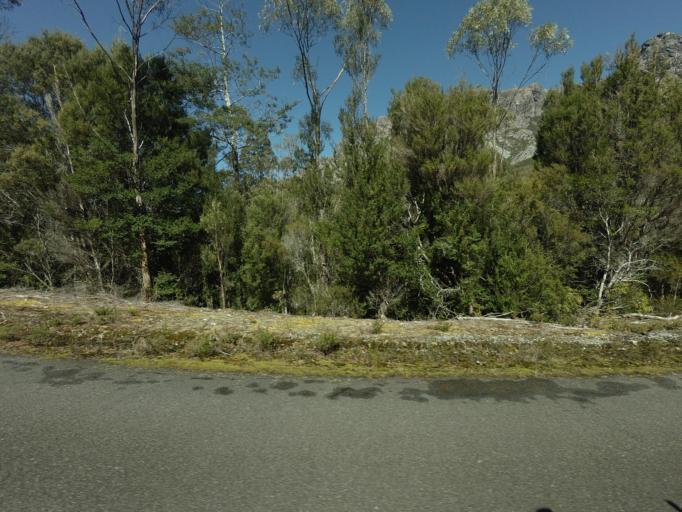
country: AU
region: Tasmania
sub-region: Huon Valley
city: Geeveston
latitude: -42.8582
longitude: 146.2304
